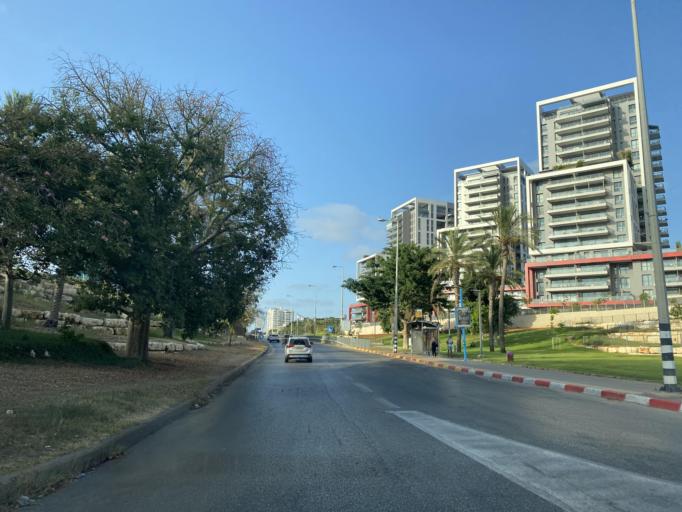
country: IL
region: Tel Aviv
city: Herzliyya
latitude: 32.1608
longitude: 34.8120
